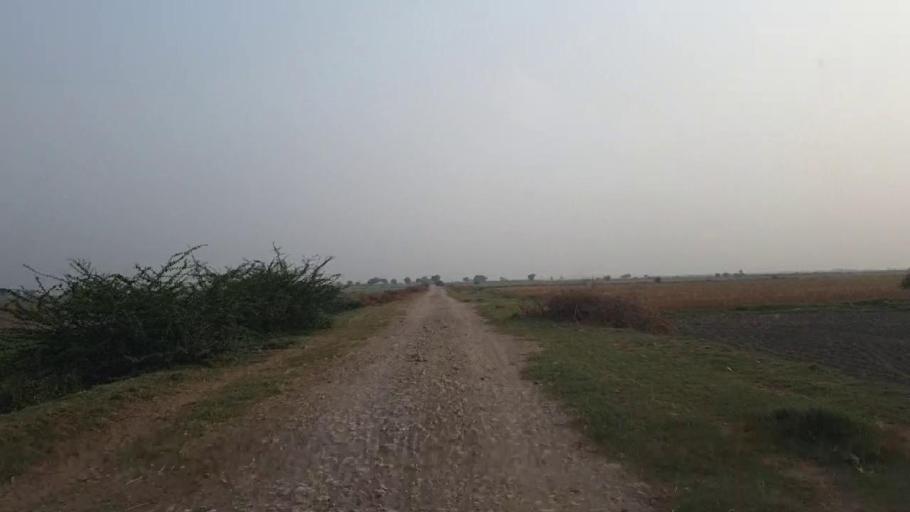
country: PK
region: Sindh
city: Mirpur Batoro
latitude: 24.6582
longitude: 68.3726
